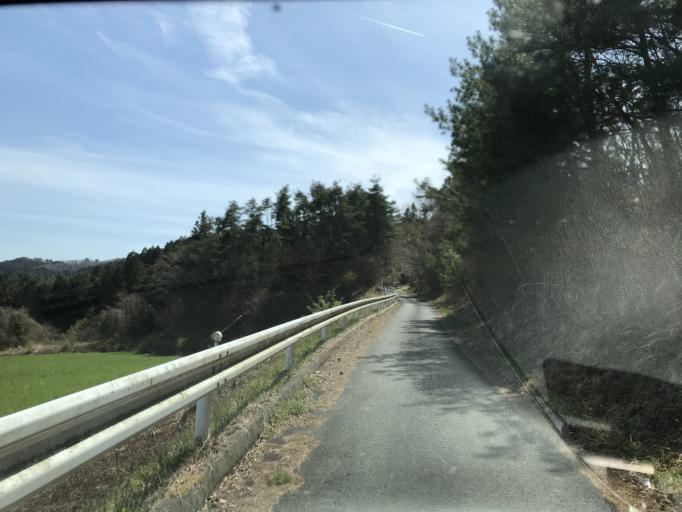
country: JP
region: Iwate
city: Ichinoseki
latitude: 38.8381
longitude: 141.2888
